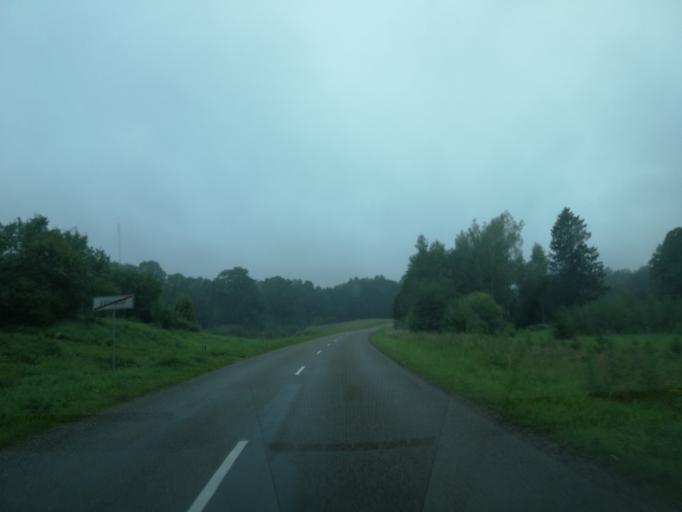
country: LV
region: Preilu Rajons
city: Jaunaglona
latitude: 56.2688
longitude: 27.0364
